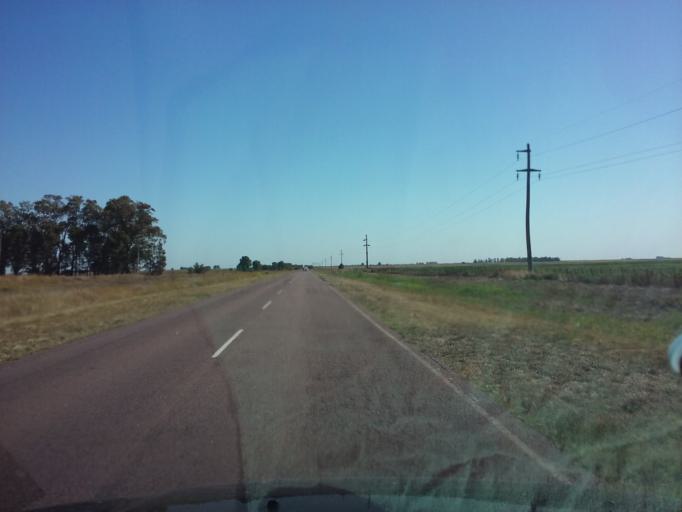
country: AR
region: La Pampa
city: Colonia Baron
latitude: -36.2506
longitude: -63.9428
